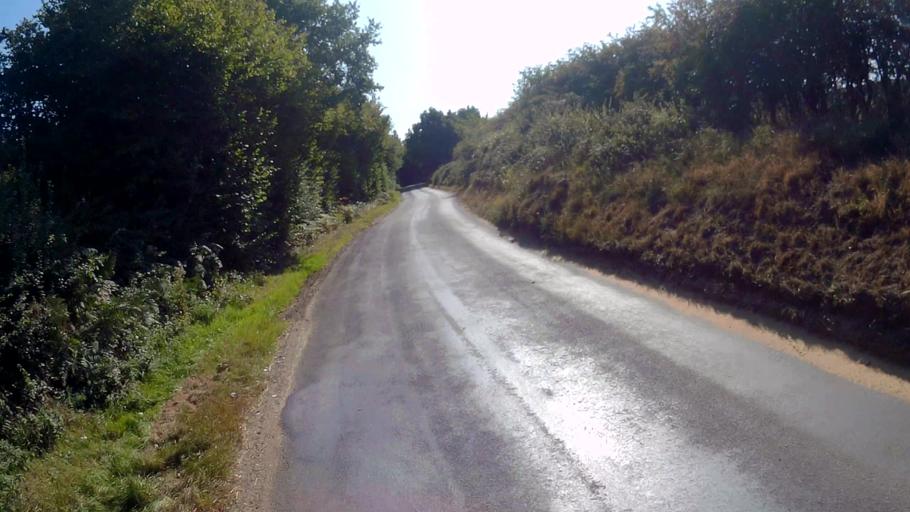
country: GB
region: England
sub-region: Surrey
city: Churt
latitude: 51.1603
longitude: -0.8078
